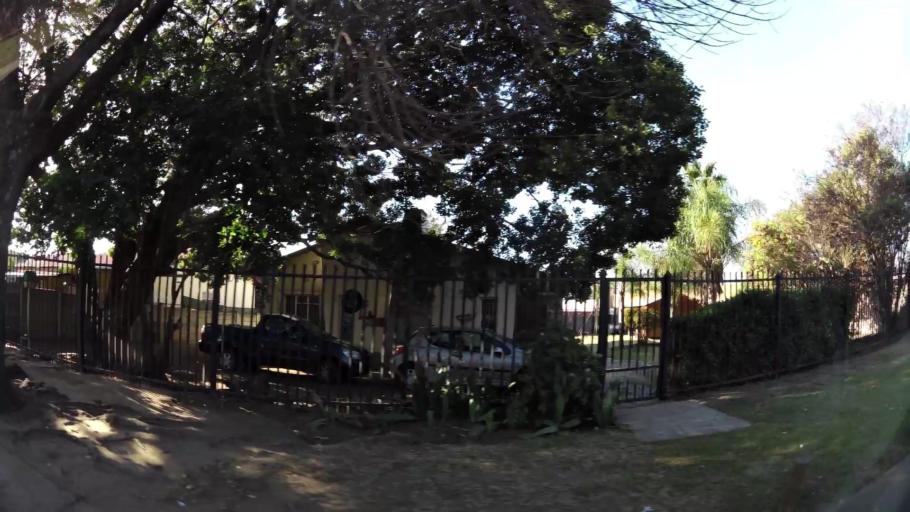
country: ZA
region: Gauteng
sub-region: City of Tshwane Metropolitan Municipality
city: Pretoria
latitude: -25.7230
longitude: 28.1569
